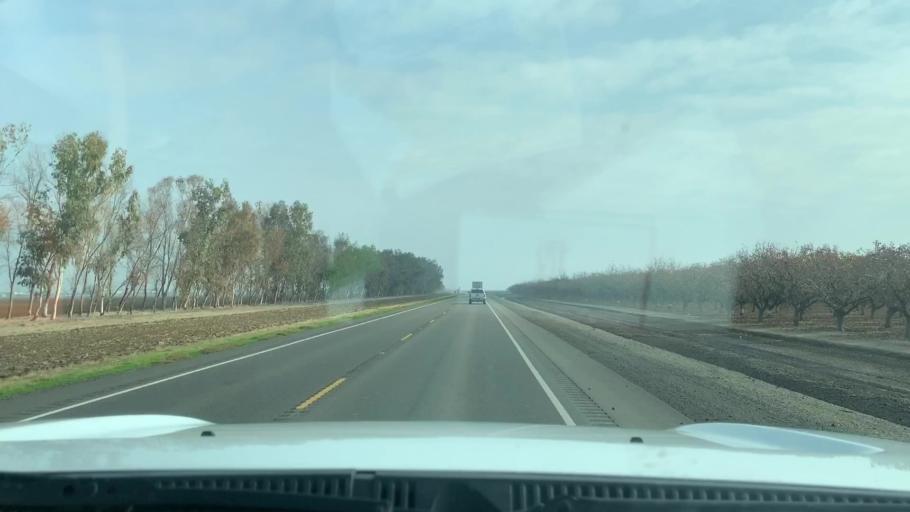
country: US
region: California
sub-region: Kings County
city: Lemoore Station
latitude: 36.2552
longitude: -119.9283
